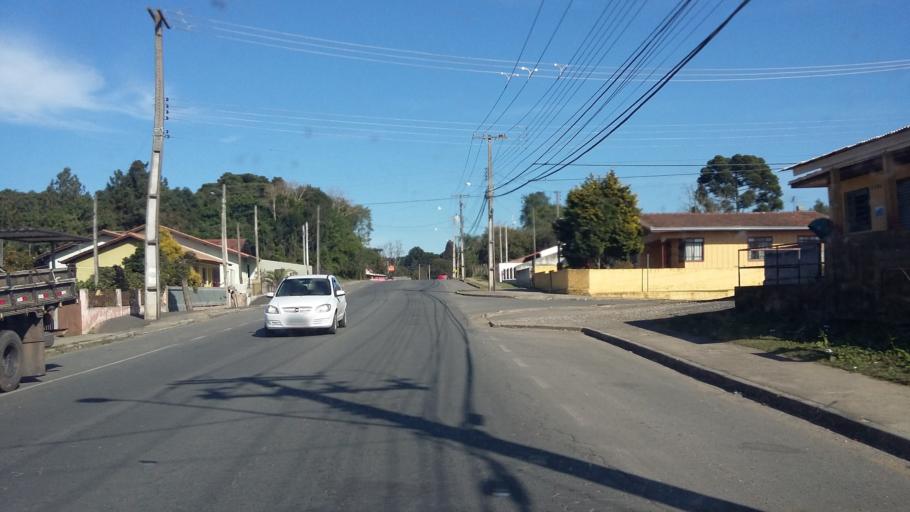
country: BR
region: Parana
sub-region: Campo Largo
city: Campo Largo
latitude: -25.4580
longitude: -49.5456
